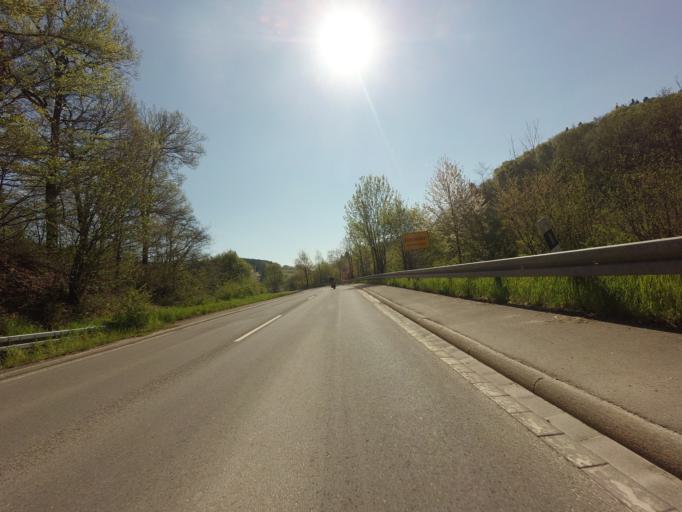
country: DE
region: North Rhine-Westphalia
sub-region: Regierungsbezirk Arnsberg
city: Drolshagen
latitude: 51.0806
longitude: 7.7900
